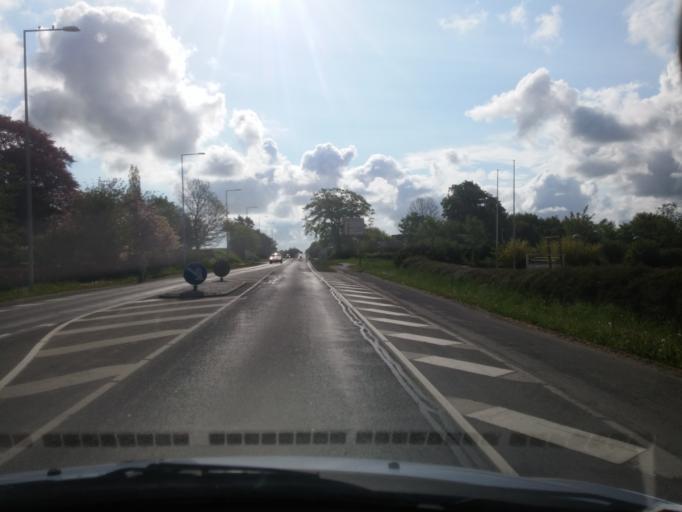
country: DK
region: South Denmark
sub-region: Nyborg Kommune
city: Ullerslev
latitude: 55.3623
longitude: 10.6751
